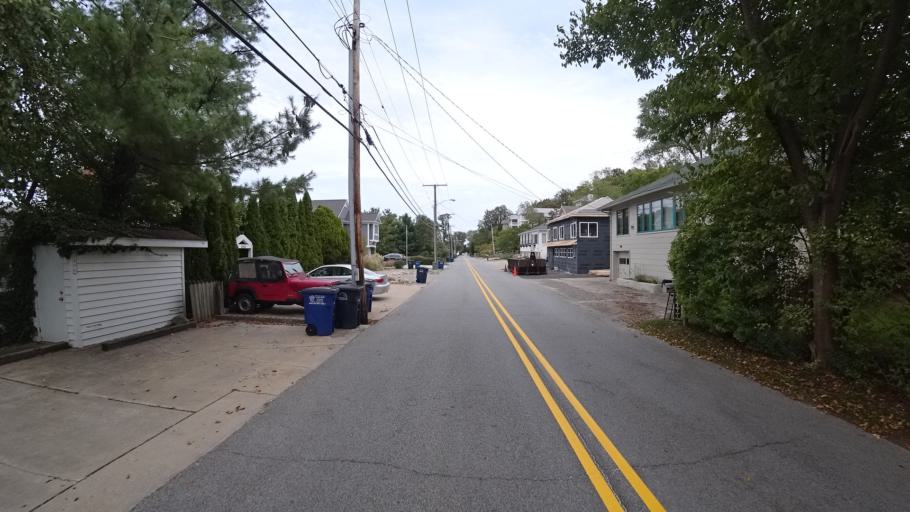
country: US
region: Indiana
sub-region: LaPorte County
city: Long Beach
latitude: 41.7350
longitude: -86.8787
